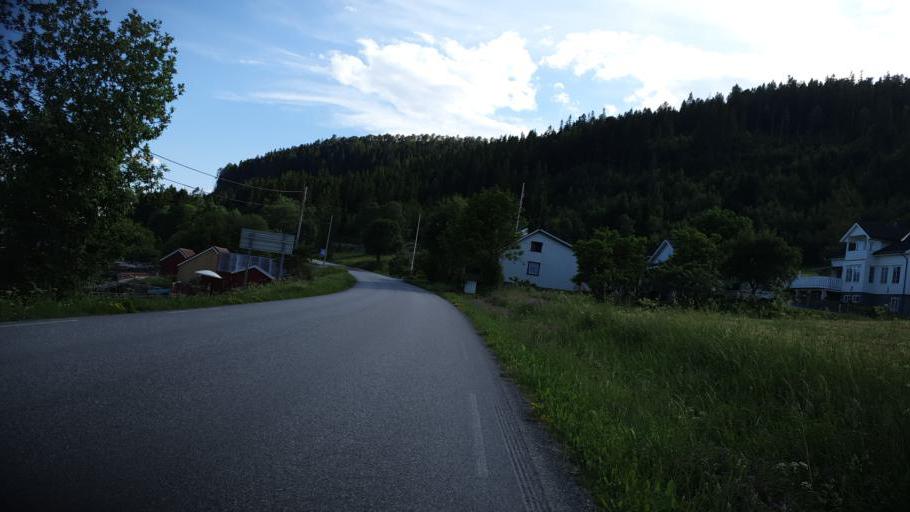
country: NO
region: Sor-Trondelag
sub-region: Trondheim
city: Trondheim
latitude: 63.5816
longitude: 10.4170
